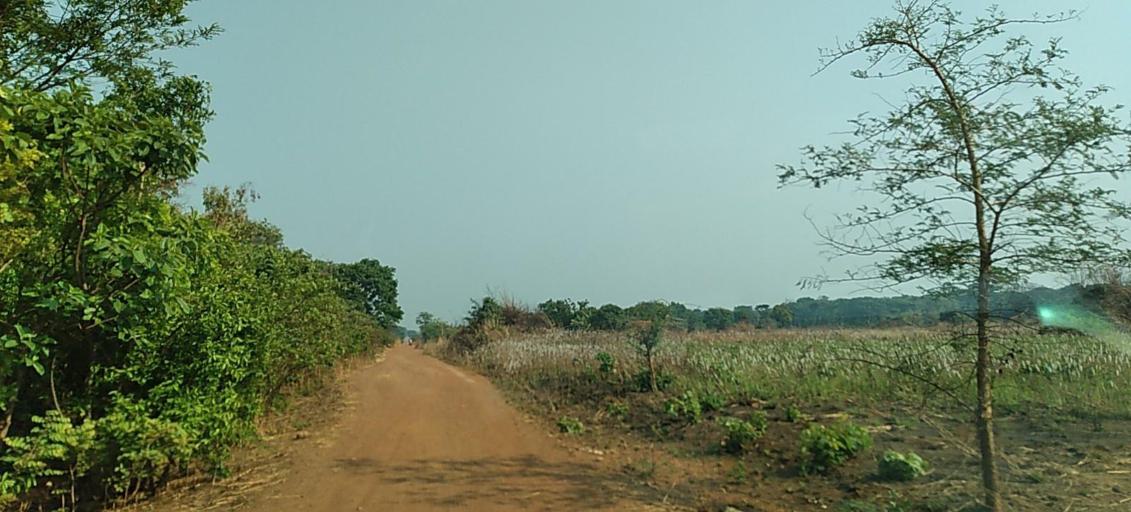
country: ZM
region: Copperbelt
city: Chingola
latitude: -12.8344
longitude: 27.5417
